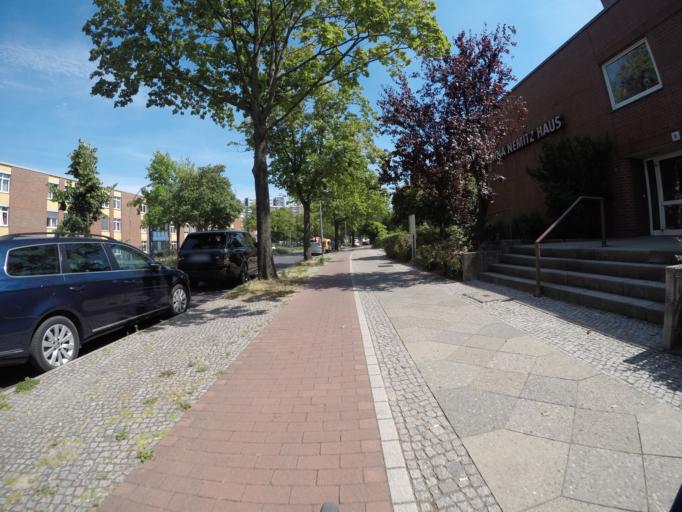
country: DE
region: Berlin
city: Buckow
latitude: 52.4340
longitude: 13.4567
